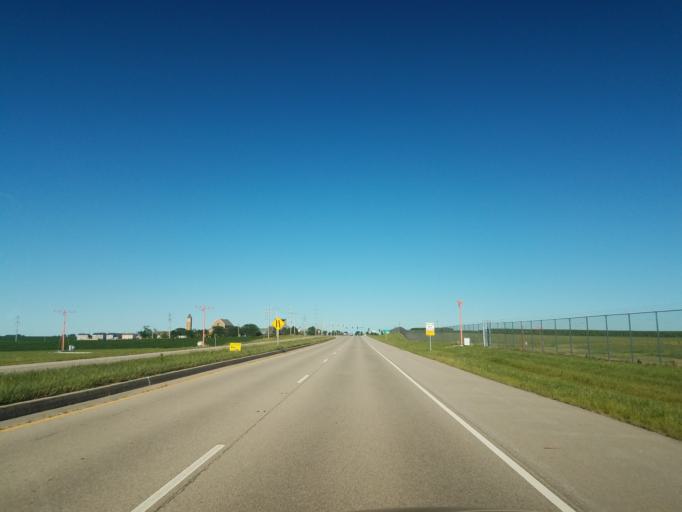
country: US
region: Illinois
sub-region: McLean County
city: Bloomington
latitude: 40.4881
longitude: -88.9068
